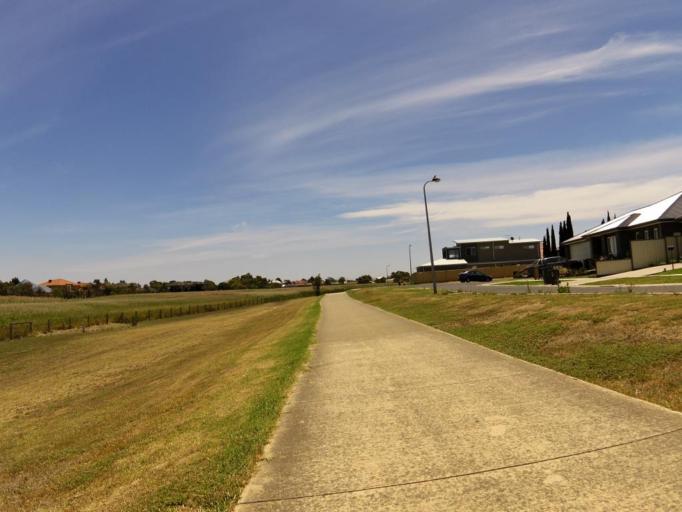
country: AU
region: Victoria
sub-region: Hobsons Bay
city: Altona Meadows
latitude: -37.8821
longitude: 144.7663
